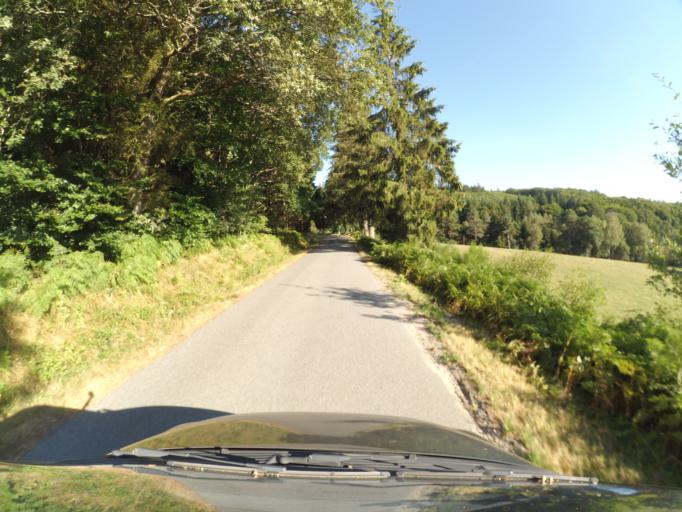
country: FR
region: Limousin
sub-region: Departement de la Creuse
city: Banize
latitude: 45.7709
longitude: 1.9942
